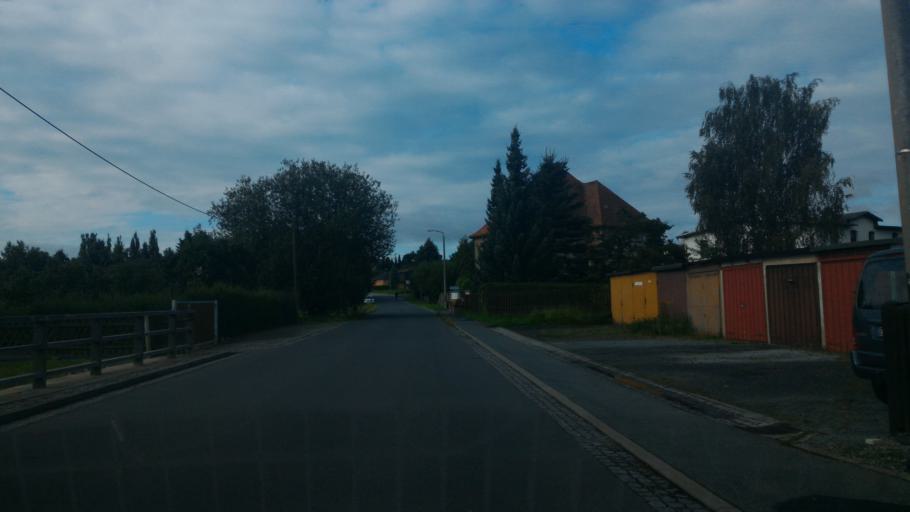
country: DE
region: Saxony
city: Neugersdorf
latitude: 50.9744
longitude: 14.6165
